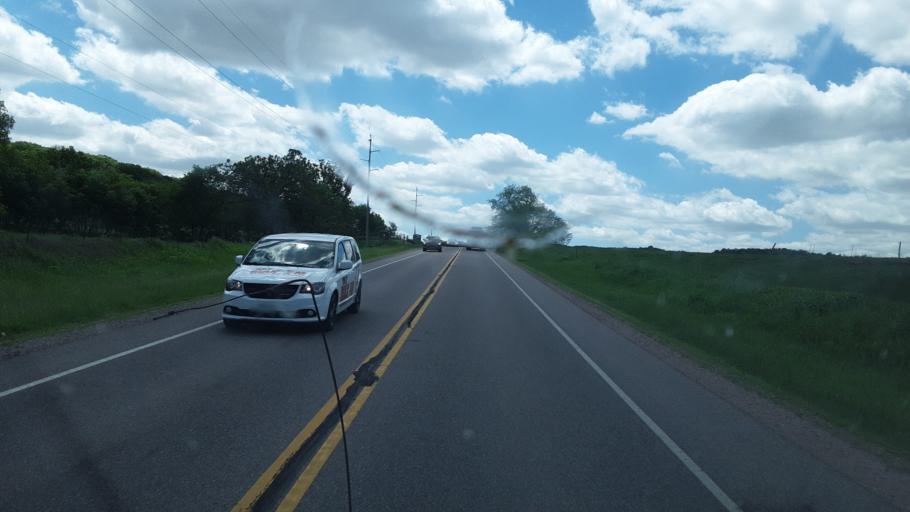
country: US
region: Wisconsin
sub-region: Sauk County
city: Reedsburg
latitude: 43.5925
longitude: -89.9447
